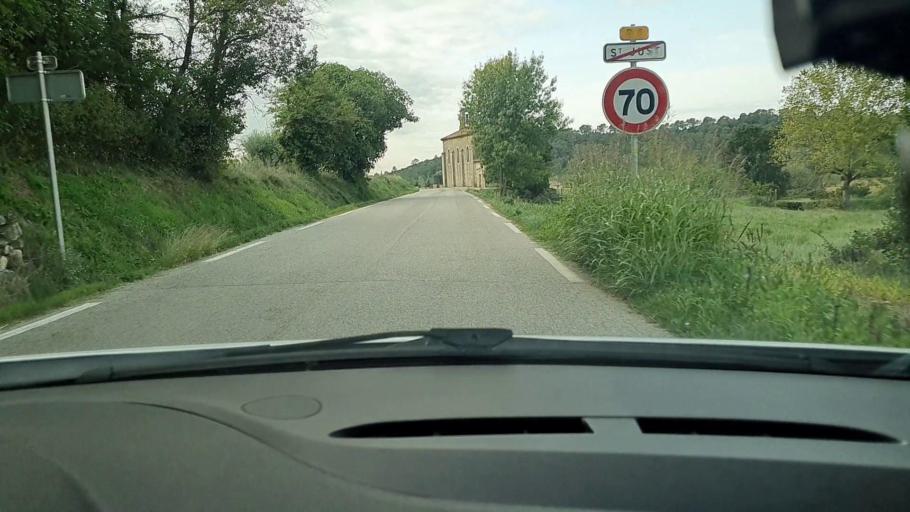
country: FR
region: Languedoc-Roussillon
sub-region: Departement du Gard
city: Mons
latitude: 44.1106
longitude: 4.2247
